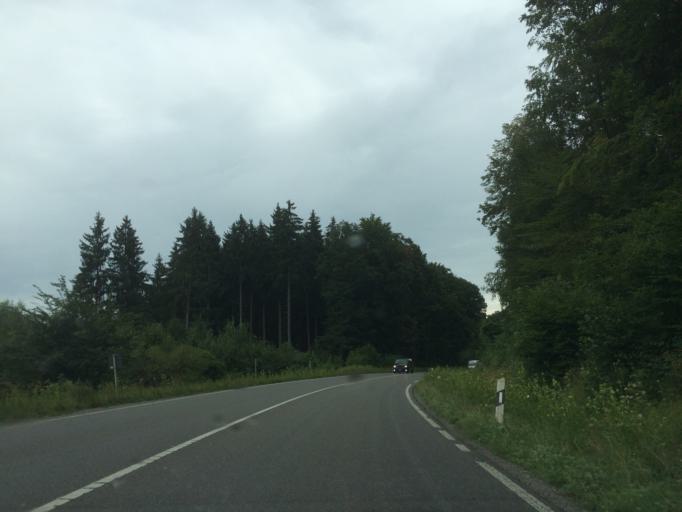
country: DE
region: Baden-Wuerttemberg
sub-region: Tuebingen Region
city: Baindt
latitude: 47.8708
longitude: 9.6939
